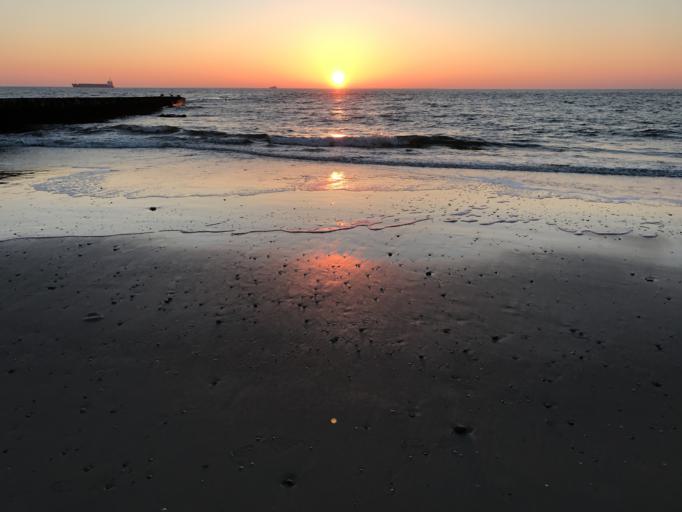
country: DE
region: Lower Saxony
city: Borkum
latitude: 53.5768
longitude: 6.6651
